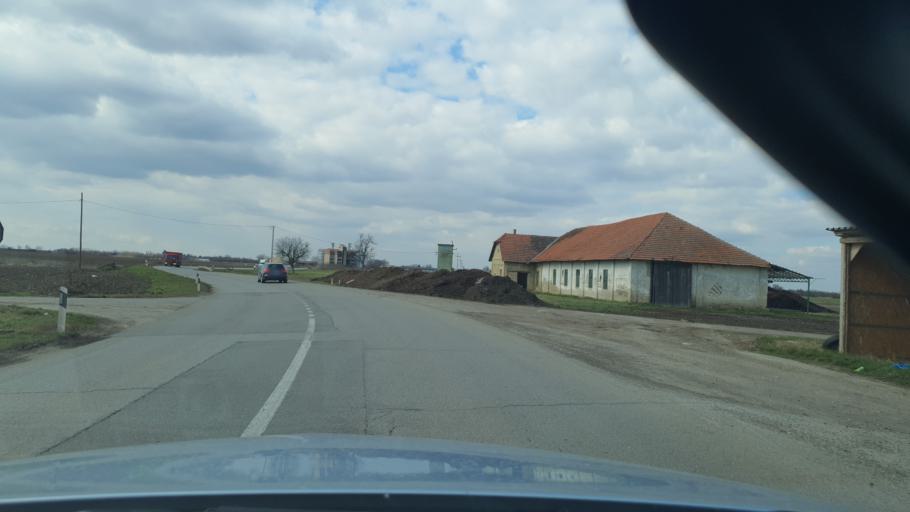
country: RS
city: Maglic
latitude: 45.3906
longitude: 19.4851
